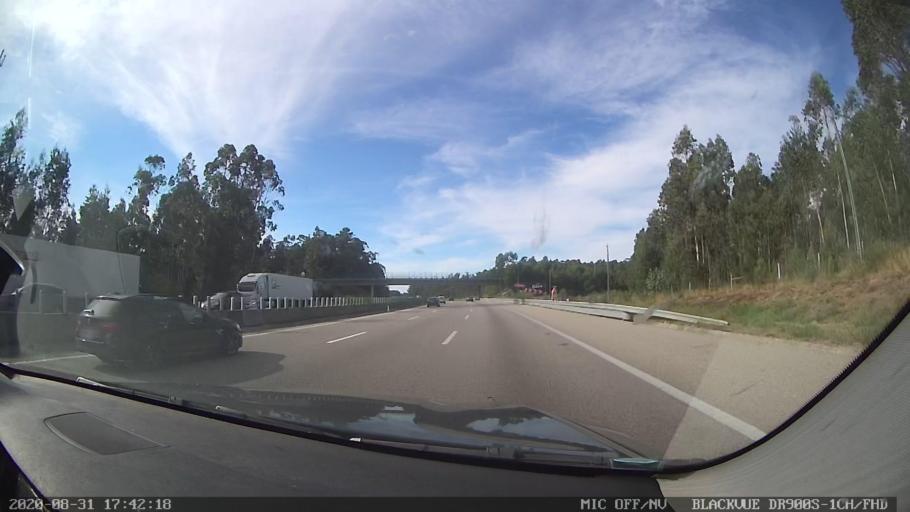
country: PT
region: Aveiro
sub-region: Ovar
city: Valega
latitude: 40.8558
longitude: -8.5533
